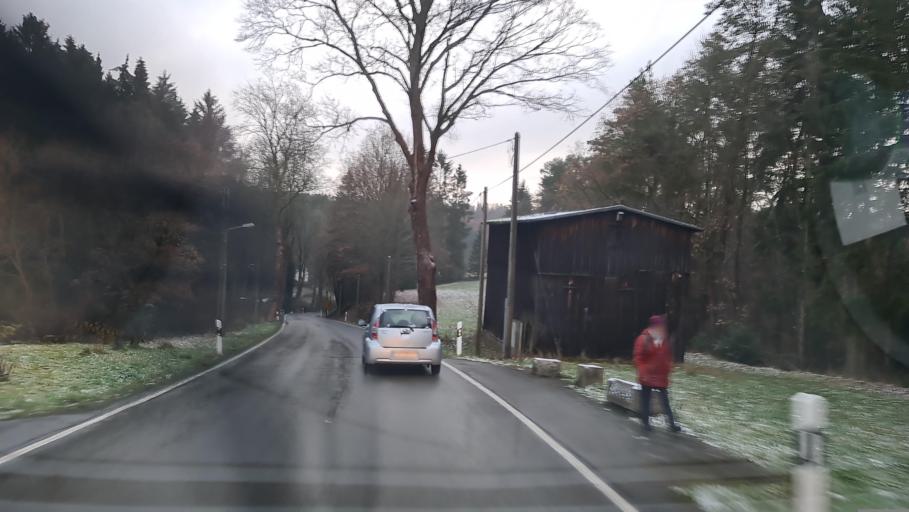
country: DE
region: Saxony
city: Mylau
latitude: 50.5967
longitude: 12.2834
